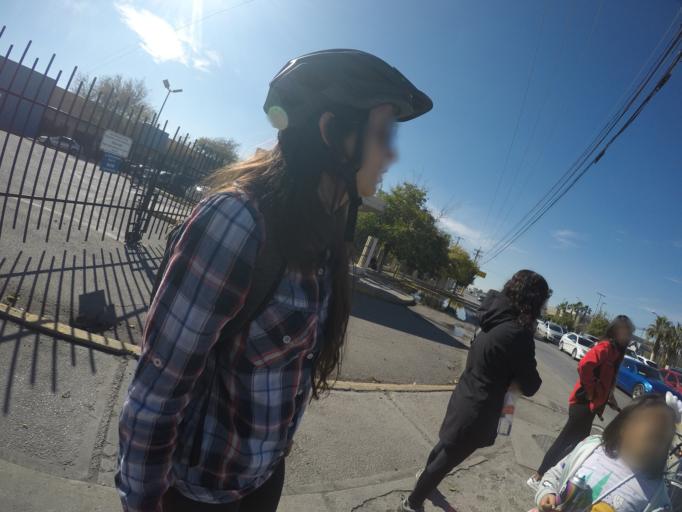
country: MX
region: Chihuahua
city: Ciudad Juarez
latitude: 31.7329
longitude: -106.4149
